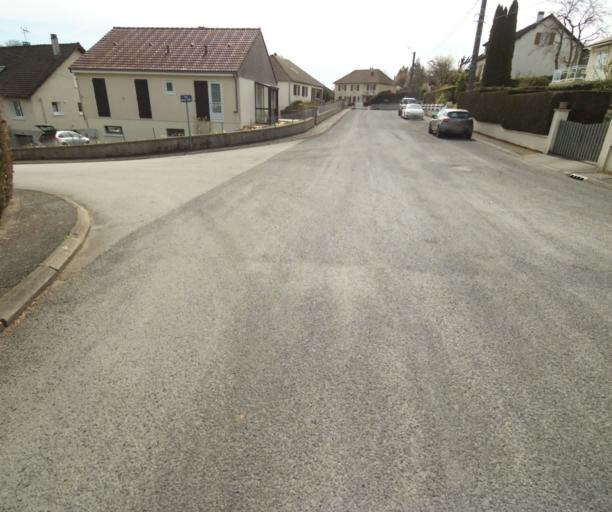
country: FR
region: Limousin
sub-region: Departement de la Correze
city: Naves
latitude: 45.3113
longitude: 1.7683
